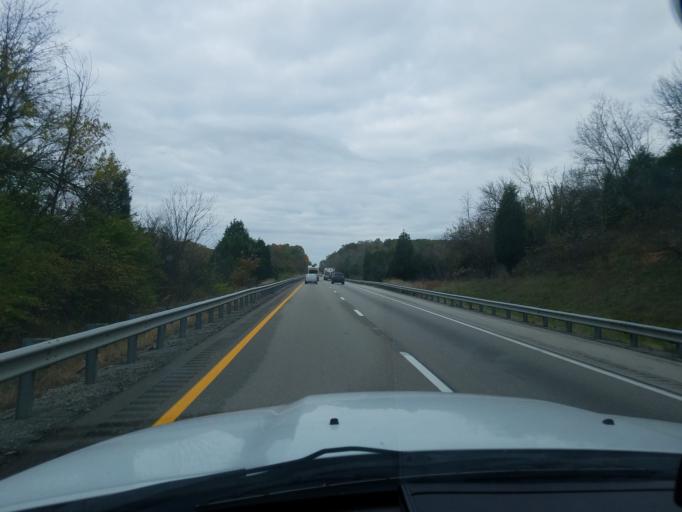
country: US
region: Indiana
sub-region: Switzerland County
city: Vevay
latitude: 38.6771
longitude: -84.9888
